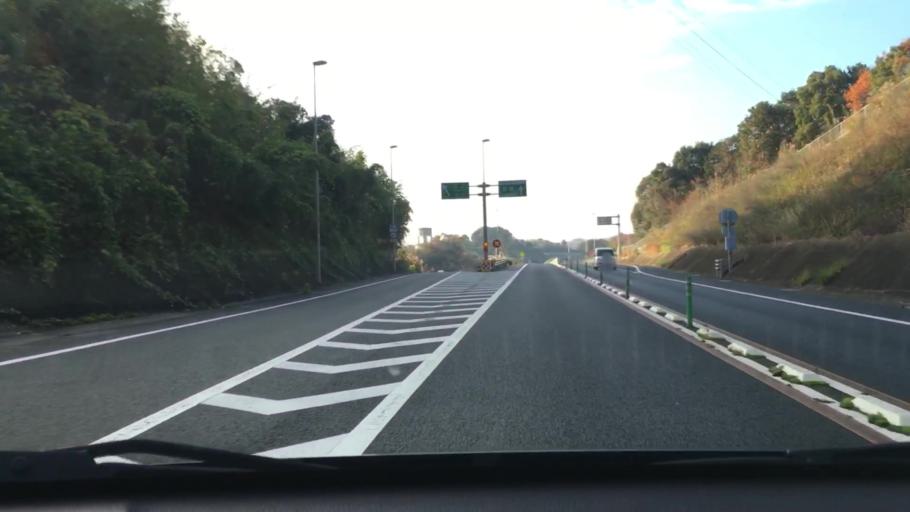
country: JP
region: Nagasaki
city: Sasebo
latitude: 33.0877
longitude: 129.7781
